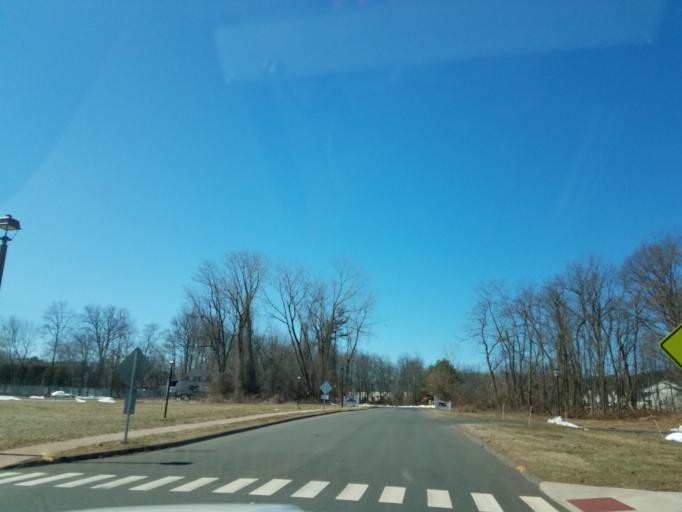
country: US
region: Connecticut
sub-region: Hartford County
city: Windsor Locks
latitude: 41.9053
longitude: -72.6364
